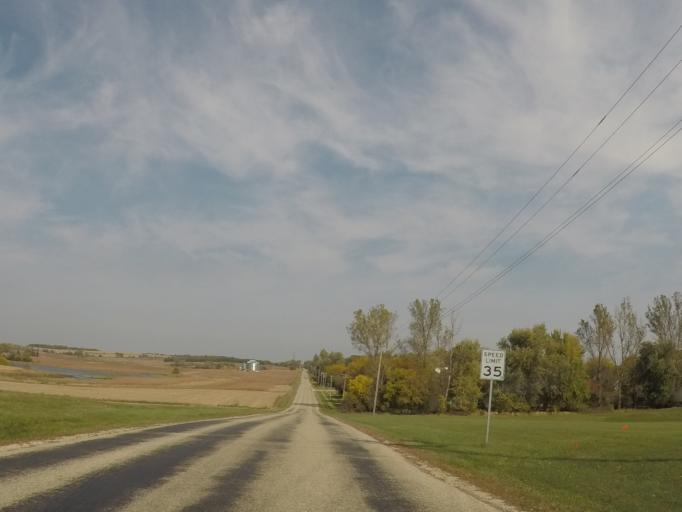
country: US
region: Wisconsin
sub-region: Dane County
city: Cross Plains
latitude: 43.0517
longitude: -89.6010
